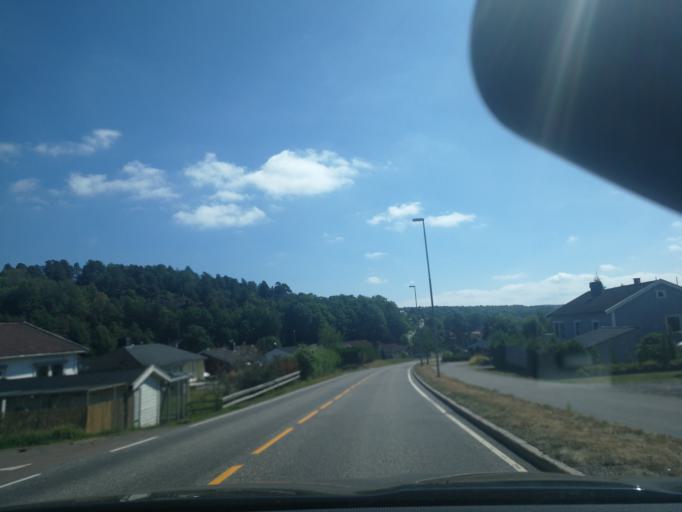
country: NO
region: Vestfold
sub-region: Stokke
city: Melsomvik
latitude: 59.2286
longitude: 10.3273
